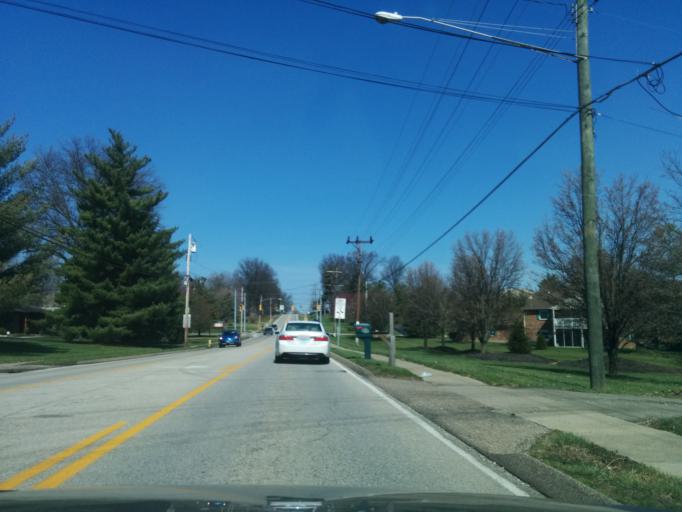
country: US
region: Ohio
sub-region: Hamilton County
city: Groesbeck
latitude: 39.2303
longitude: -84.5992
